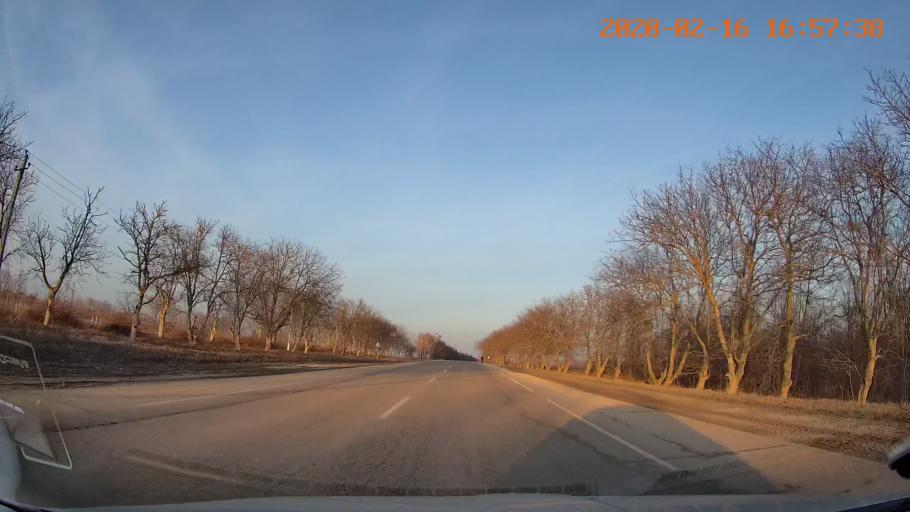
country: MD
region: Briceni
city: Briceni
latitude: 48.3444
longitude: 27.0709
